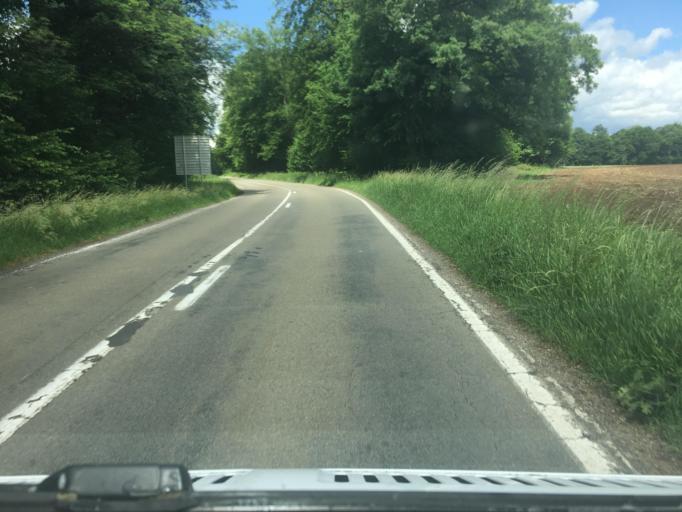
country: BE
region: Wallonia
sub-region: Province du Luxembourg
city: Florenville
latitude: 49.6754
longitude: 5.3398
